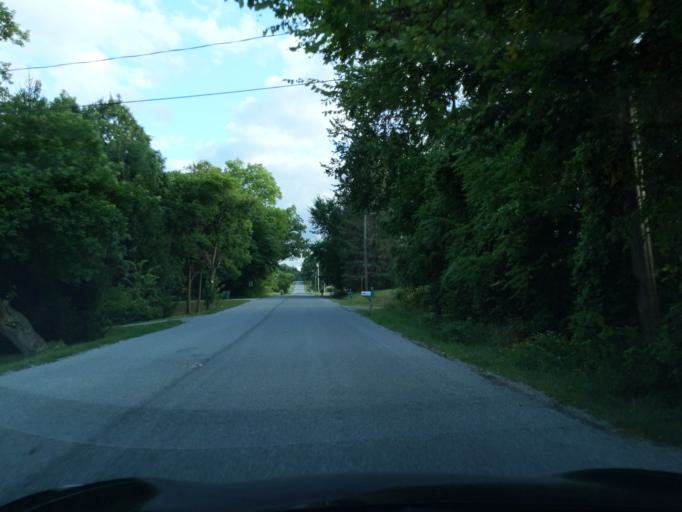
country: US
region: Michigan
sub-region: Ingham County
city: Holt
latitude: 42.6177
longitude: -84.5824
